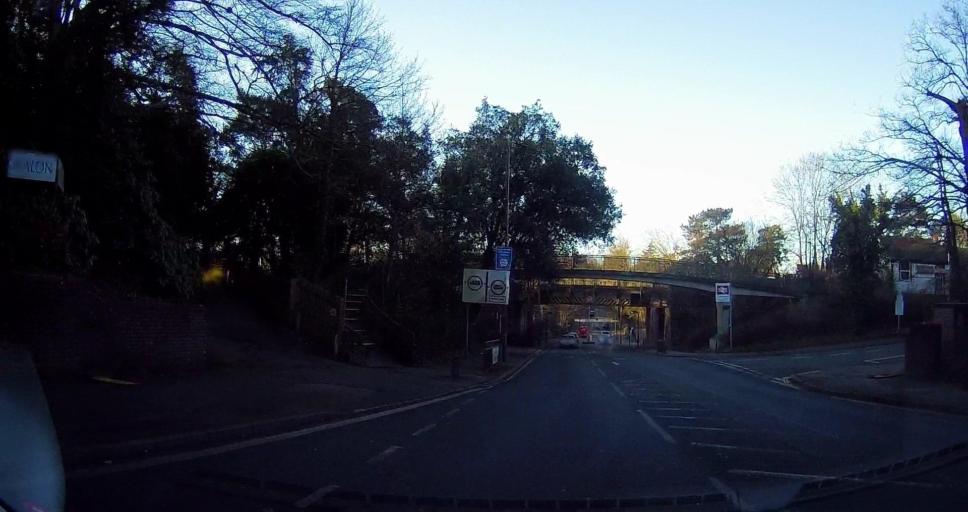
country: GB
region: England
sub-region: Greater London
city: Chislehurst
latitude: 51.4053
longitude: 0.0595
